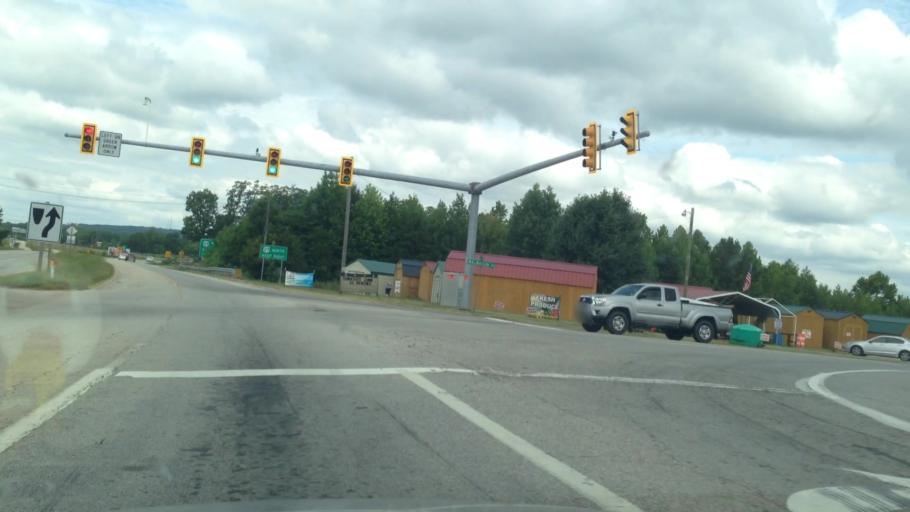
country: US
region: Virginia
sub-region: Pittsylvania County
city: Mount Hermon
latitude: 36.6968
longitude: -79.3667
